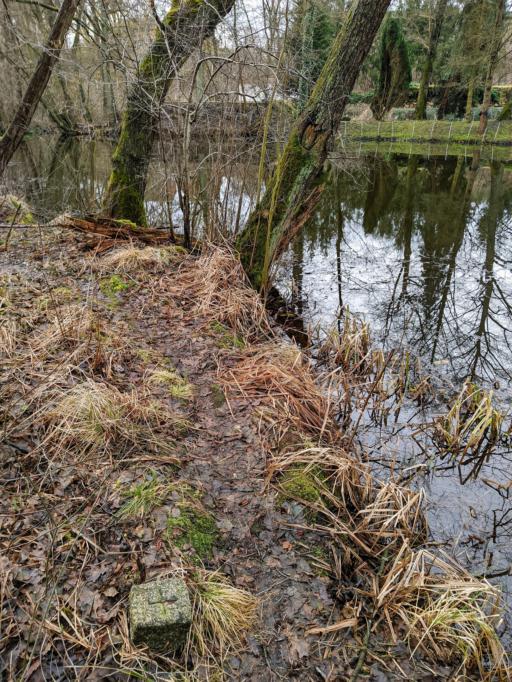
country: PL
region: Lubusz
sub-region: Powiat swiebodzinski
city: Miedzylesie
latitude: 52.1189
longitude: 15.4144
